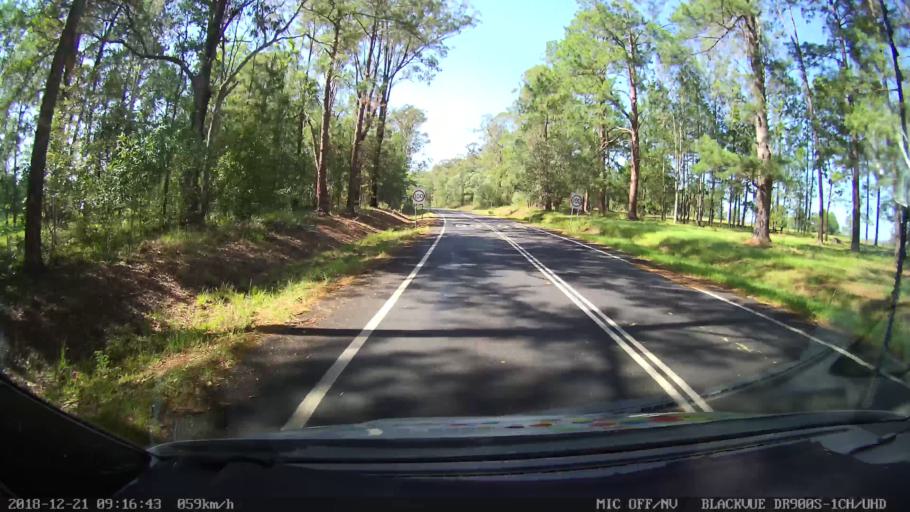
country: AU
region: New South Wales
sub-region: Clarence Valley
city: Maclean
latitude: -29.2846
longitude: 152.9889
